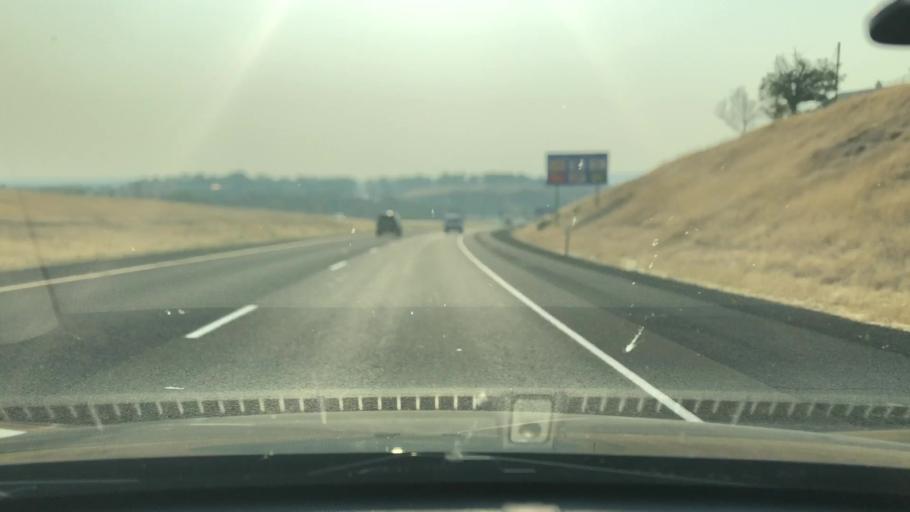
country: US
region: Oregon
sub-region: Umatilla County
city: Pendleton
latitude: 45.6612
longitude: -118.7960
